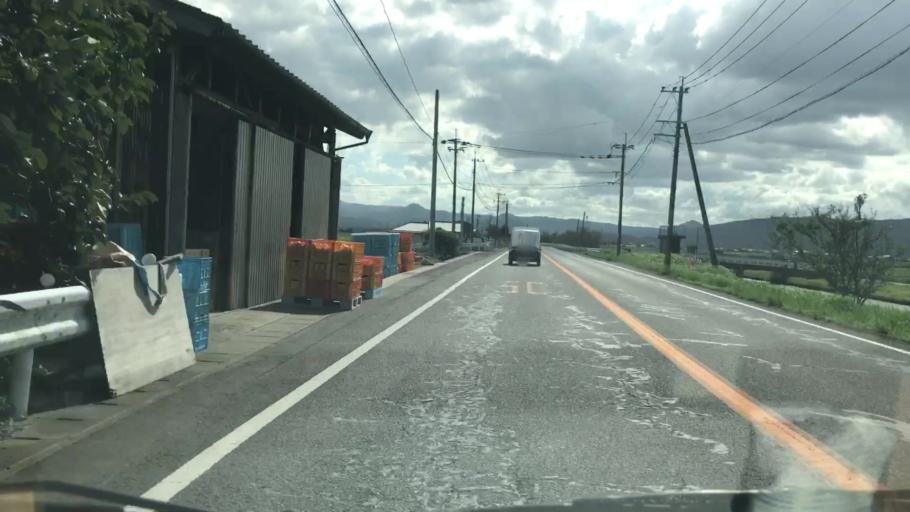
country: JP
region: Saga Prefecture
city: Kashima
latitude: 33.1579
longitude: 130.1620
